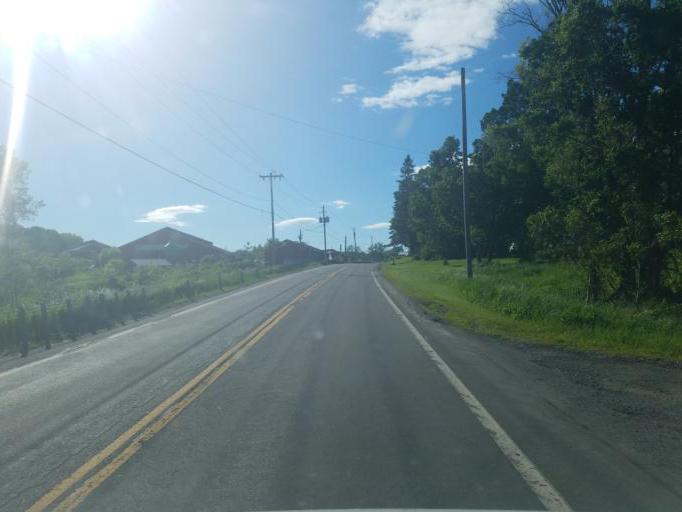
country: US
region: New York
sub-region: Herkimer County
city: Little Falls
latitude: 43.0100
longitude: -74.7968
